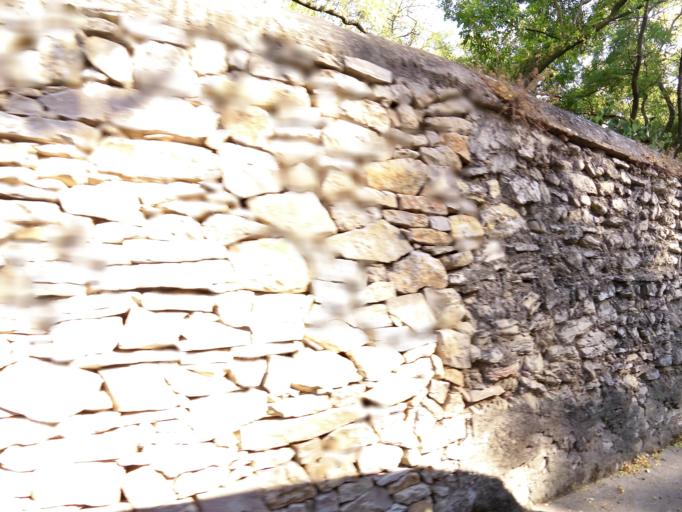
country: FR
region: Languedoc-Roussillon
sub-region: Departement du Gard
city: Nimes
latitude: 43.8512
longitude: 4.3700
